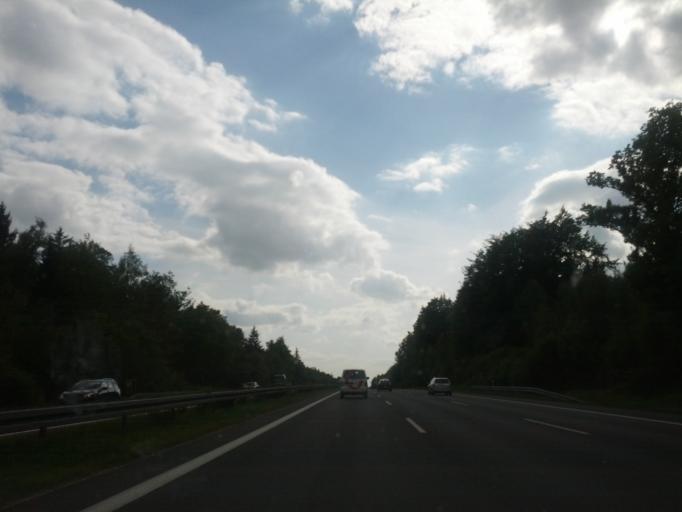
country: DE
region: Saxony
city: Nossen
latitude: 51.0192
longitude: 13.2533
